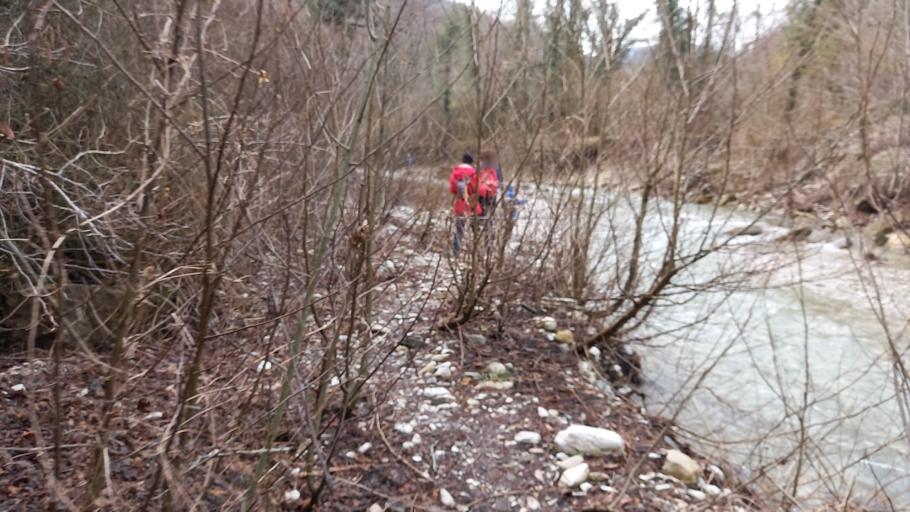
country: RU
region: Krasnodarskiy
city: Dzhubga
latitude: 44.4109
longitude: 38.7173
